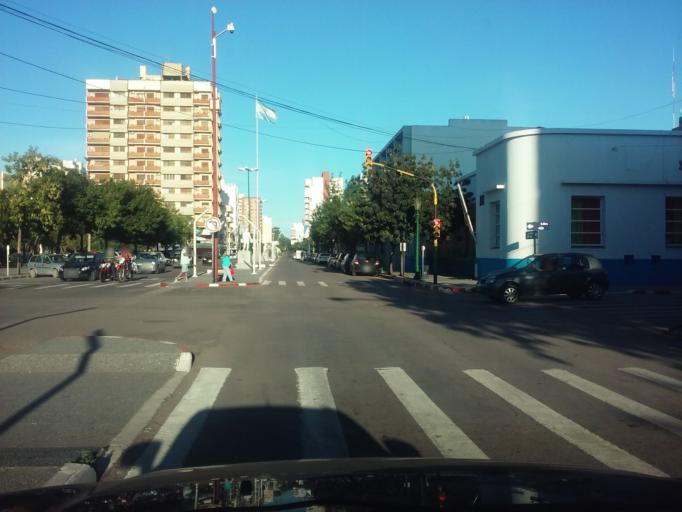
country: AR
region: La Pampa
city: Santa Rosa
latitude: -36.6210
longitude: -64.2914
